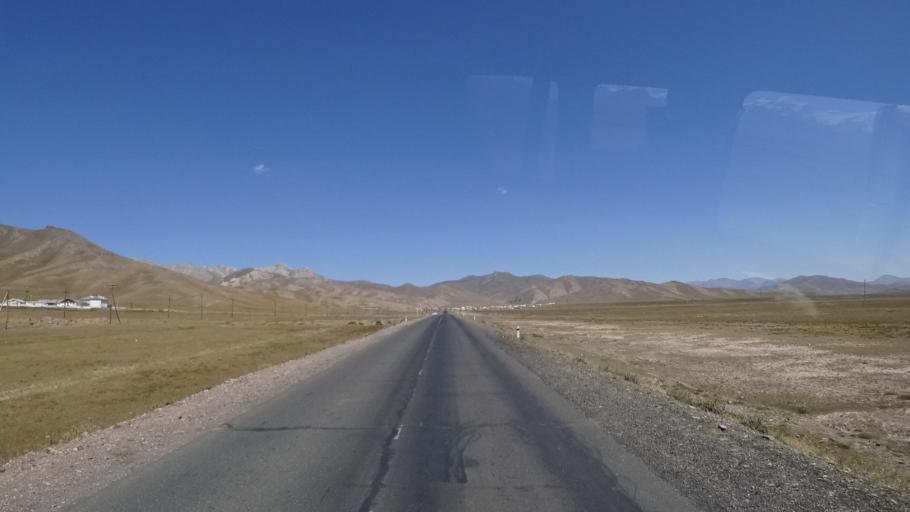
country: KG
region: Osh
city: Gul'cha
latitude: 39.7096
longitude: 73.2335
